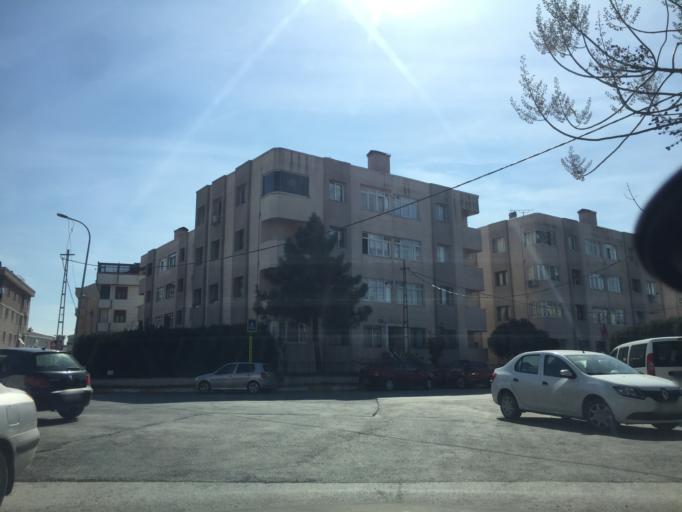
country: TR
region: Istanbul
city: Icmeler
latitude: 40.8277
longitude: 29.3191
